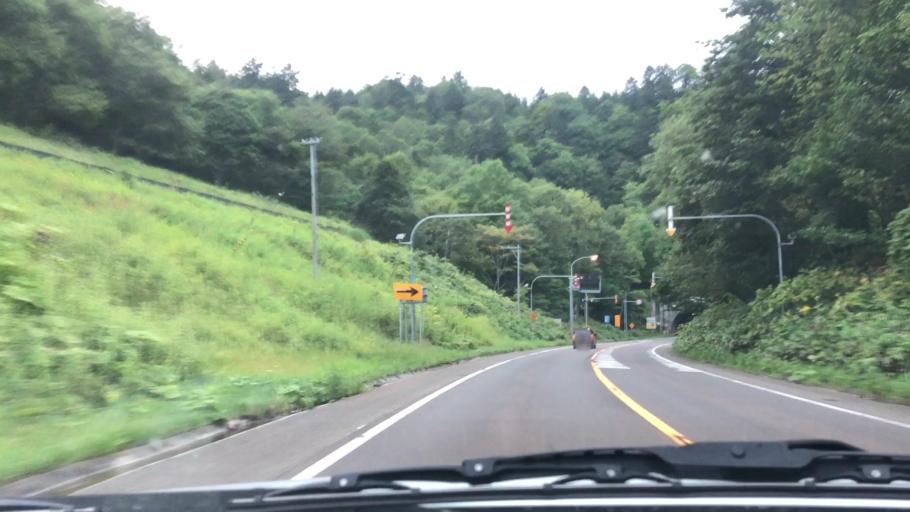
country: JP
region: Hokkaido
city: Iwamizawa
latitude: 42.9201
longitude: 142.1163
